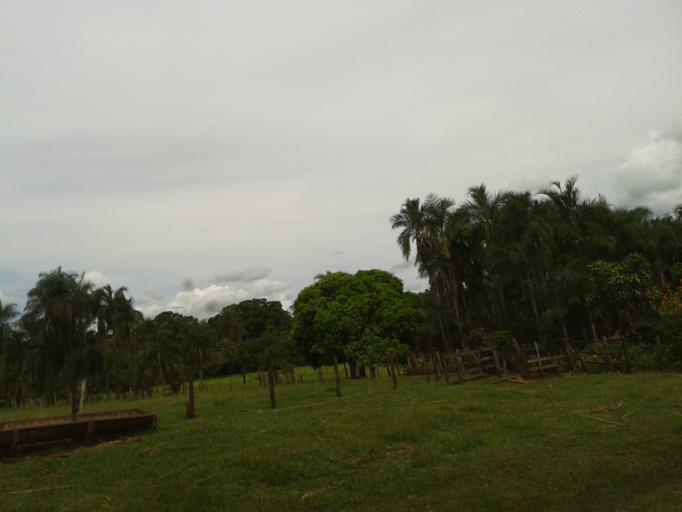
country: BR
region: Minas Gerais
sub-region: Santa Vitoria
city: Santa Vitoria
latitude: -18.8021
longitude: -49.8474
